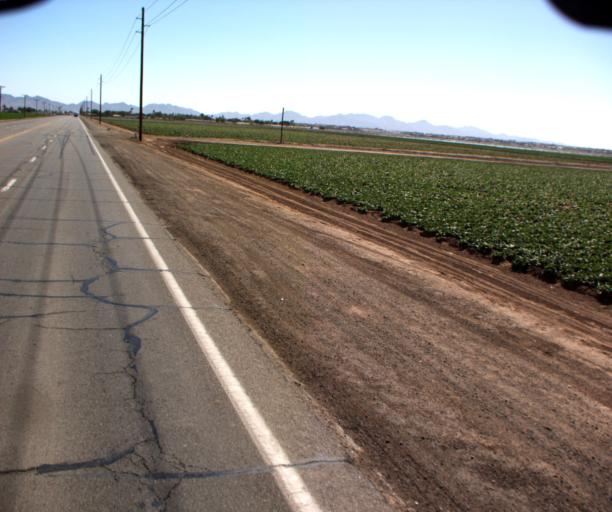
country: US
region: Arizona
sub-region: Yuma County
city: Yuma
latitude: 32.6989
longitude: -114.5569
